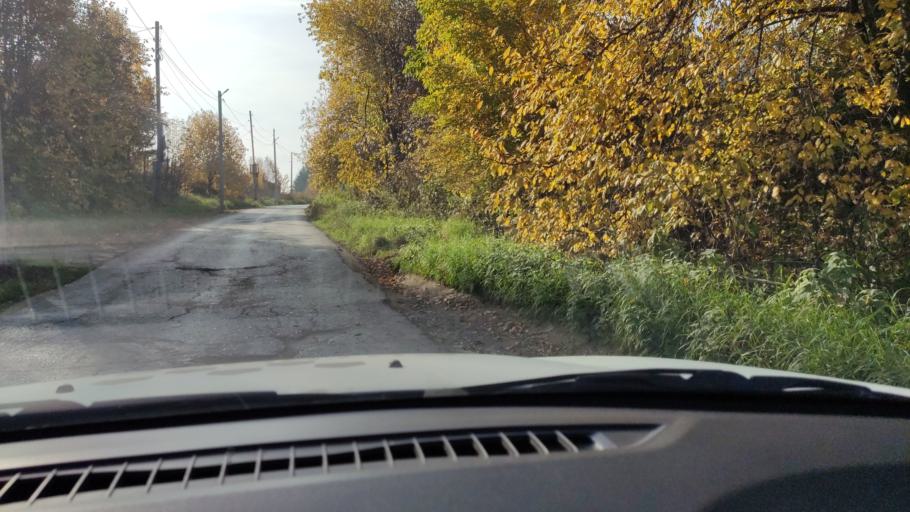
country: RU
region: Perm
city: Sylva
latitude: 58.0411
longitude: 56.7494
